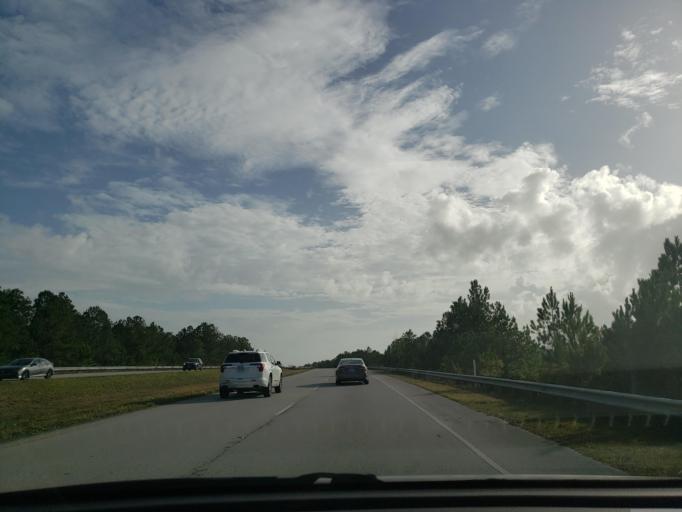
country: US
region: North Carolina
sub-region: Onslow County
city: Sneads Ferry
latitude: 34.6163
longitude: -77.4844
